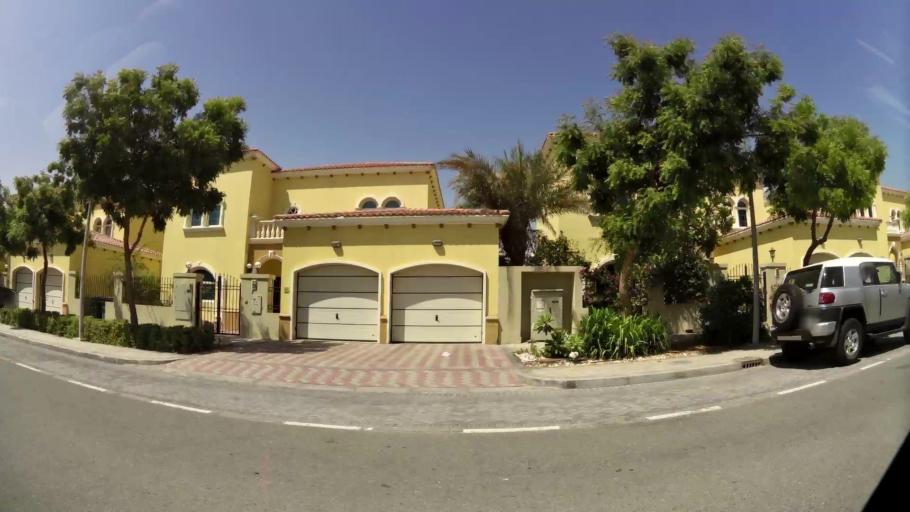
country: AE
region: Dubai
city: Dubai
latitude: 25.0496
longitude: 55.1529
